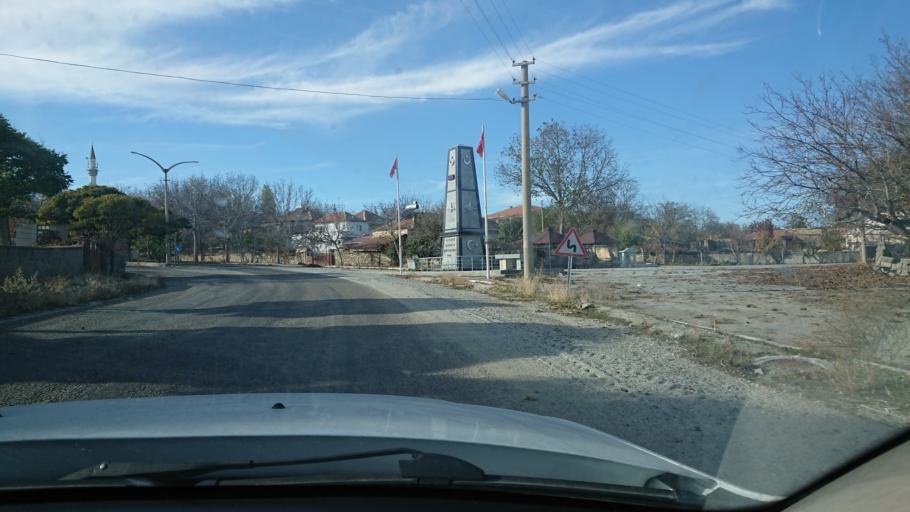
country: TR
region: Aksaray
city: Sariyahsi
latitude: 38.9593
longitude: 33.8881
